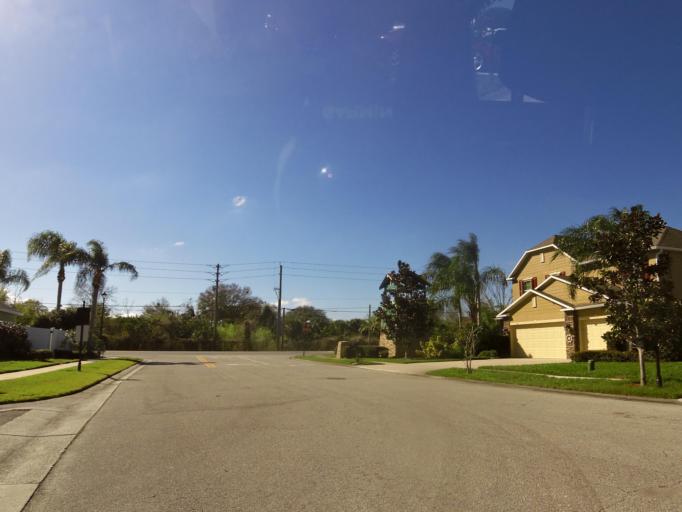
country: US
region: Florida
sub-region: Brevard County
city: Titusville
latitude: 28.5517
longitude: -80.8057
